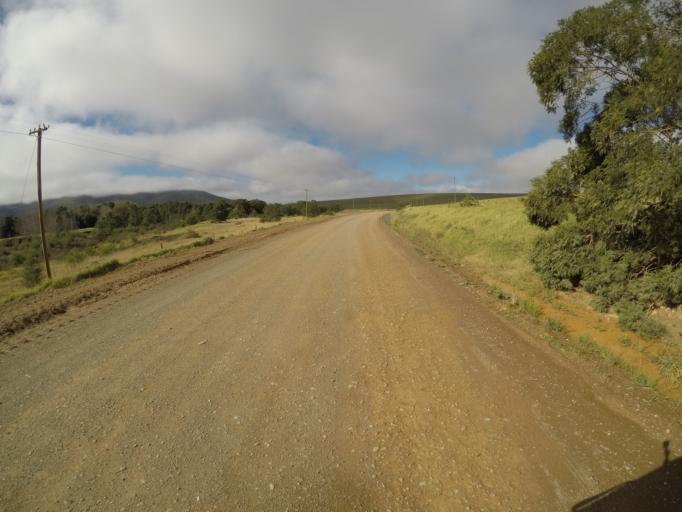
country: ZA
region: Western Cape
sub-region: Cape Winelands District Municipality
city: Ashton
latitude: -34.1288
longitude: 19.8435
